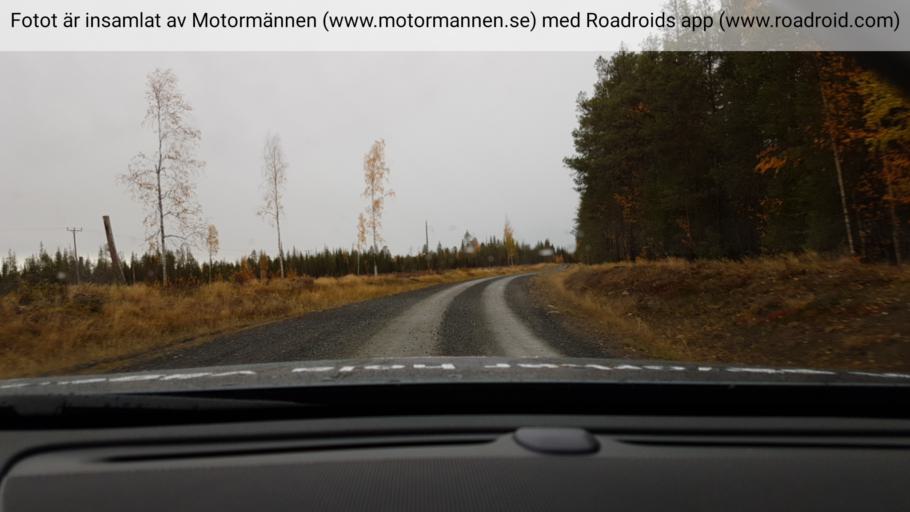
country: SE
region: Norrbotten
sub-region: Pajala Kommun
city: Pajala
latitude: 67.0069
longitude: 22.8536
